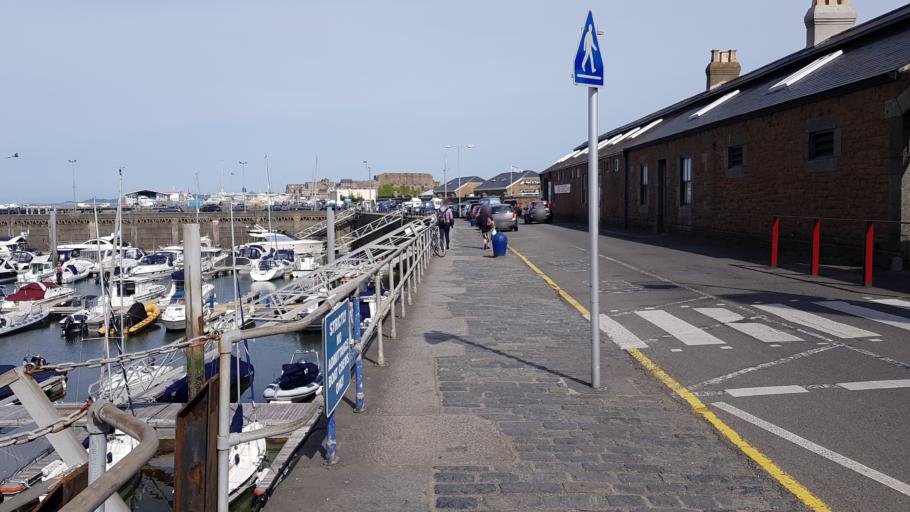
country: GG
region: St Peter Port
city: Saint Peter Port
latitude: 49.4527
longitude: -2.5352
